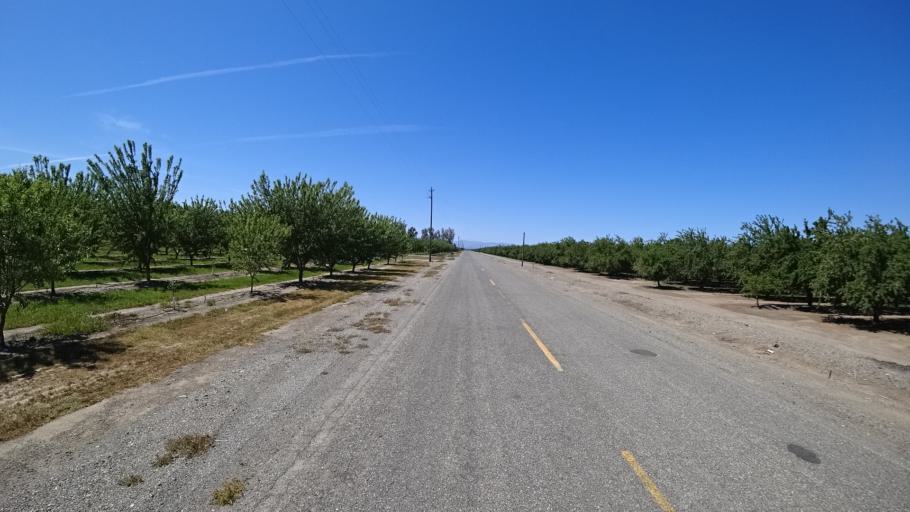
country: US
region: California
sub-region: Glenn County
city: Orland
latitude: 39.7249
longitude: -122.1149
